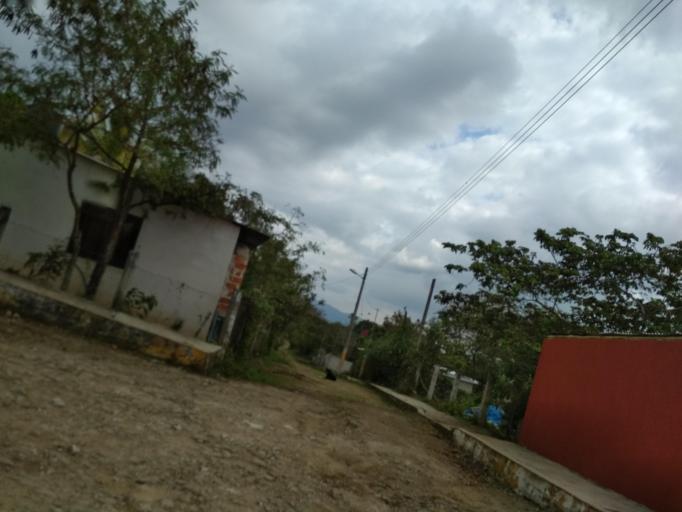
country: MX
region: Veracruz
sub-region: Coatepec
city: Tuzamapan
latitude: 19.3671
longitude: -96.8802
